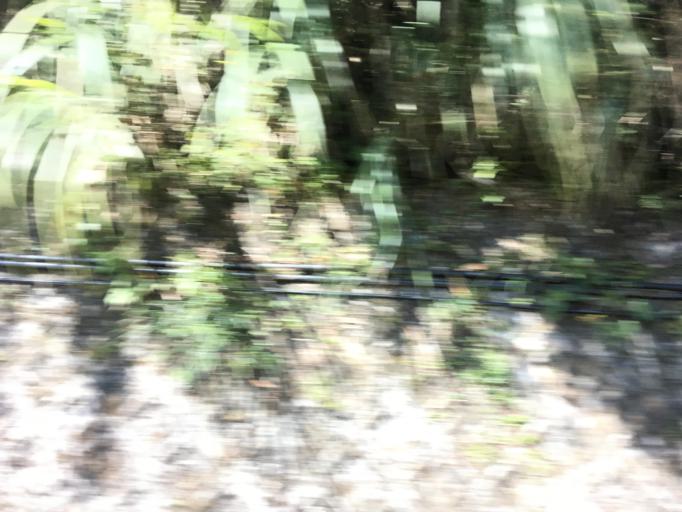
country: TW
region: Taiwan
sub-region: Yilan
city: Yilan
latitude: 24.5289
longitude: 121.5201
